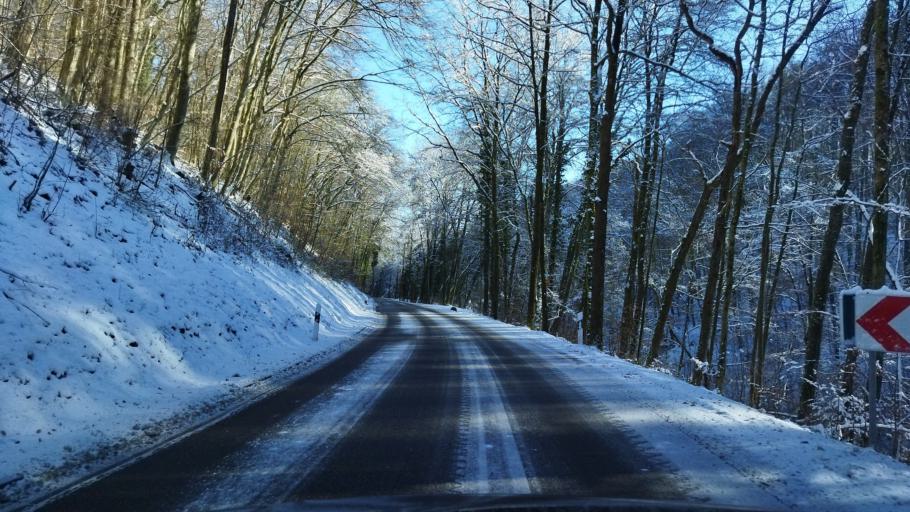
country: DE
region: Baden-Wuerttemberg
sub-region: Regierungsbezirk Stuttgart
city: Langenburg
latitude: 49.2400
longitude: 9.8952
